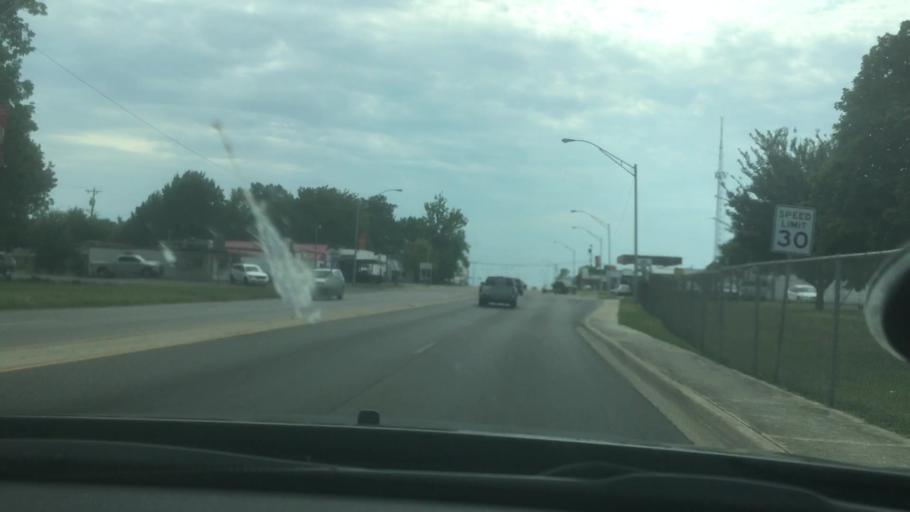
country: US
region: Oklahoma
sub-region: Pontotoc County
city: Ada
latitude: 34.7745
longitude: -96.6903
